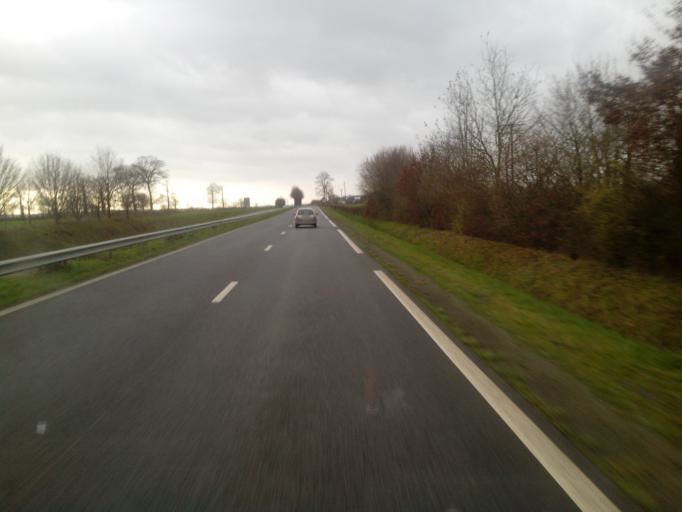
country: FR
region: Brittany
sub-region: Departement d'Ille-et-Vilaine
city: Chevaigne
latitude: 48.2189
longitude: -1.6235
